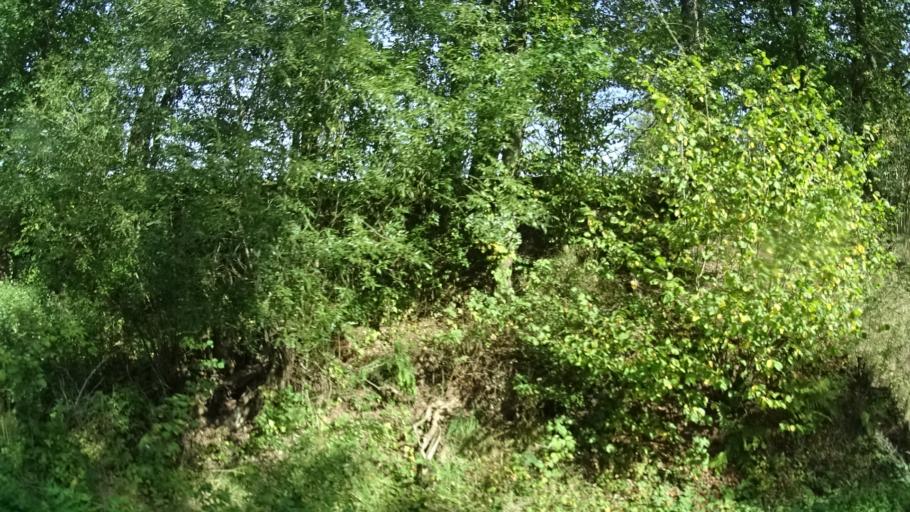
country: DE
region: Thuringia
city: Metzels
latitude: 50.6520
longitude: 10.4397
